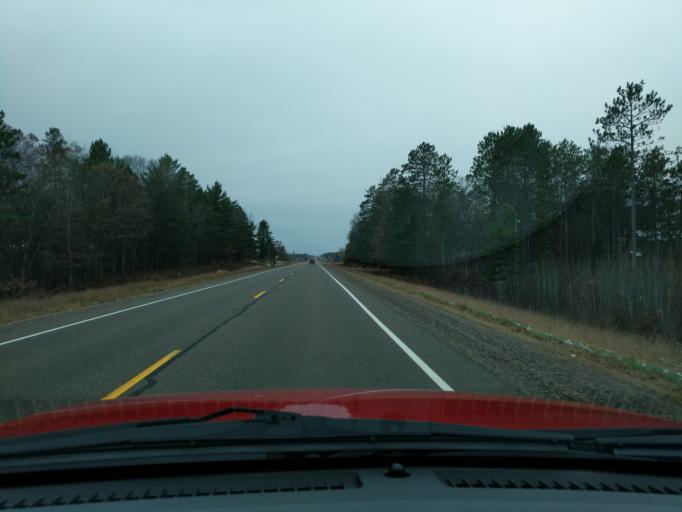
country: US
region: Wisconsin
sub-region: Washburn County
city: Shell Lake
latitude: 45.8155
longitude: -92.0898
